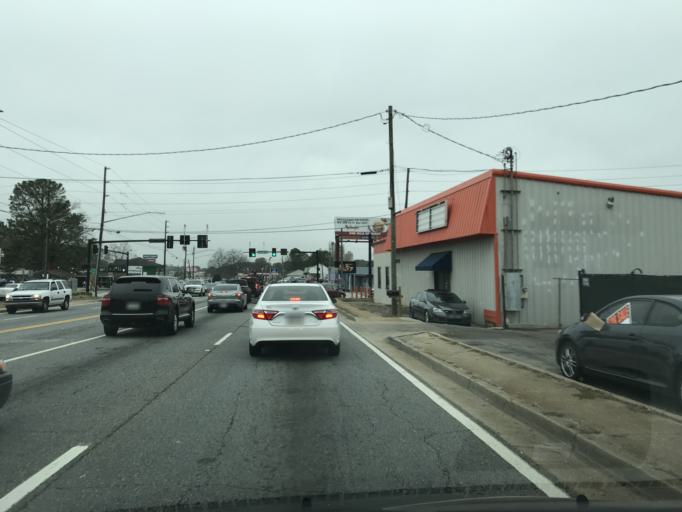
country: US
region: Georgia
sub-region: DeKalb County
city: Tucker
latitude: 33.8498
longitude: -84.2224
